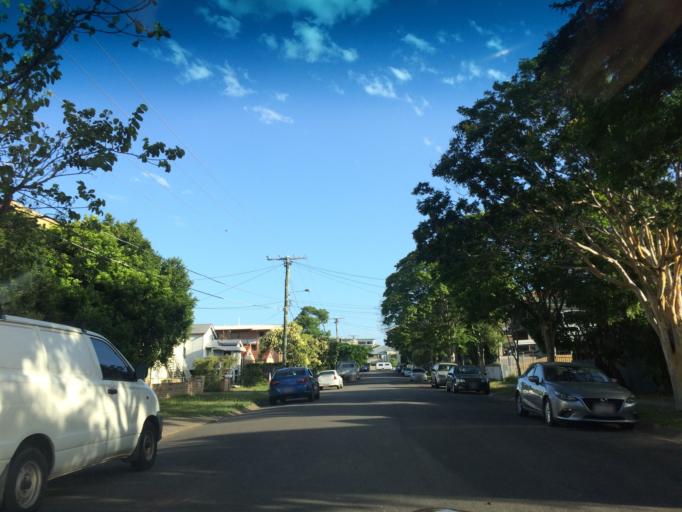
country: AU
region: Queensland
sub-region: Brisbane
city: Seven Hills
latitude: -27.4900
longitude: 153.0575
